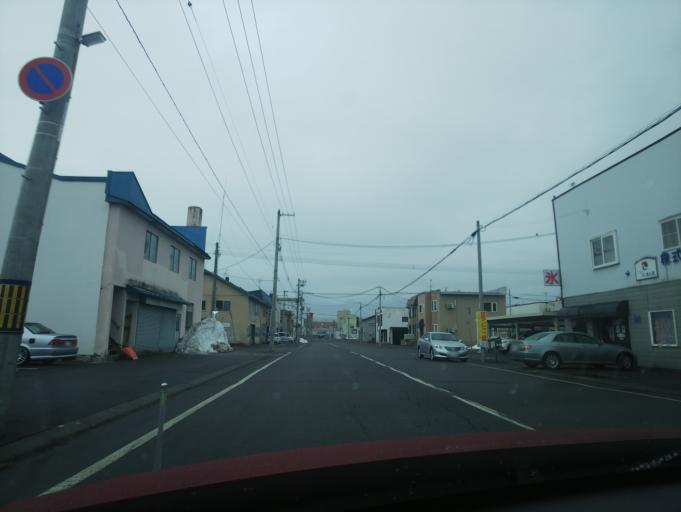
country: JP
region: Hokkaido
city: Nayoro
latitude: 44.3516
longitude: 142.4616
